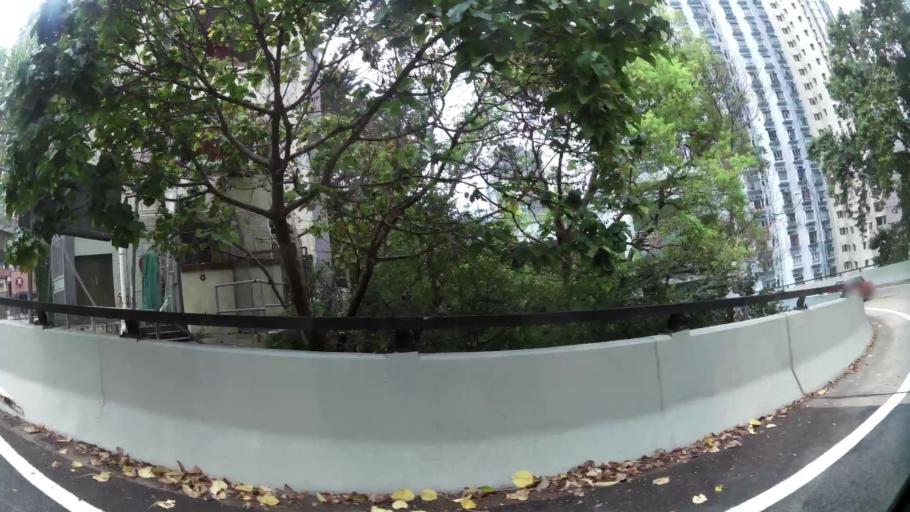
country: HK
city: Hong Kong
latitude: 22.2840
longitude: 114.1358
